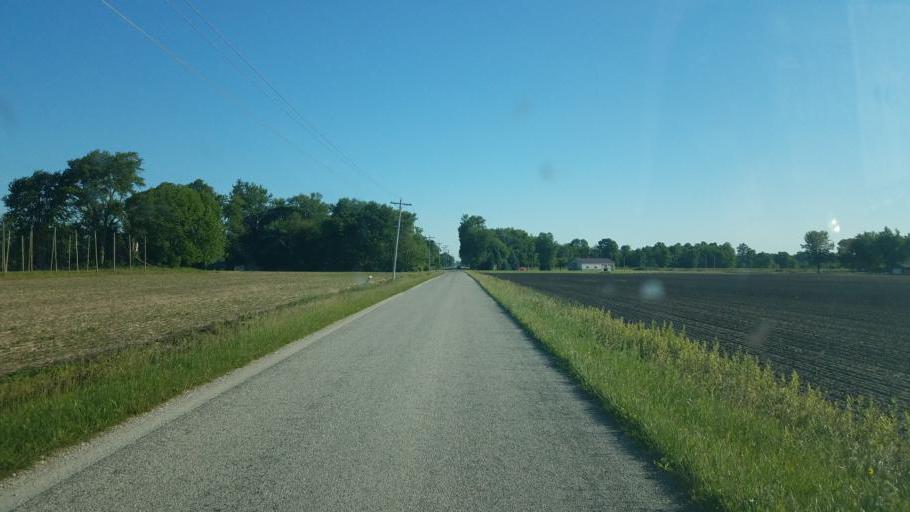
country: US
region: Ohio
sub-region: Marion County
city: Marion
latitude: 40.6268
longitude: -82.9909
